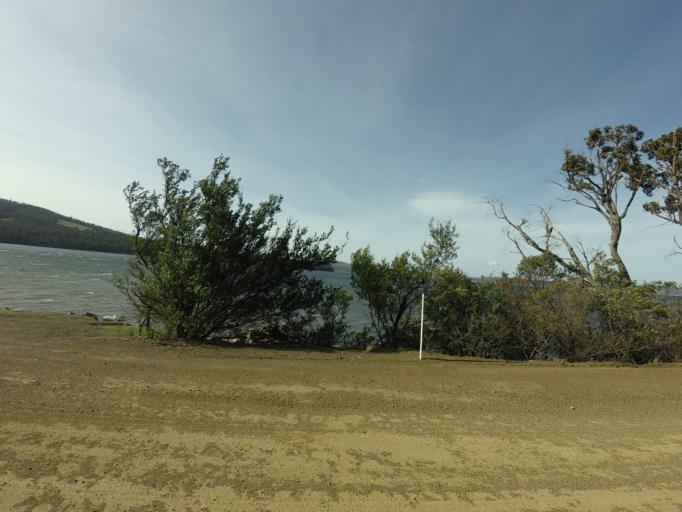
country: AU
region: Tasmania
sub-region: Kingborough
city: Kettering
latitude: -43.1149
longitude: 147.2713
